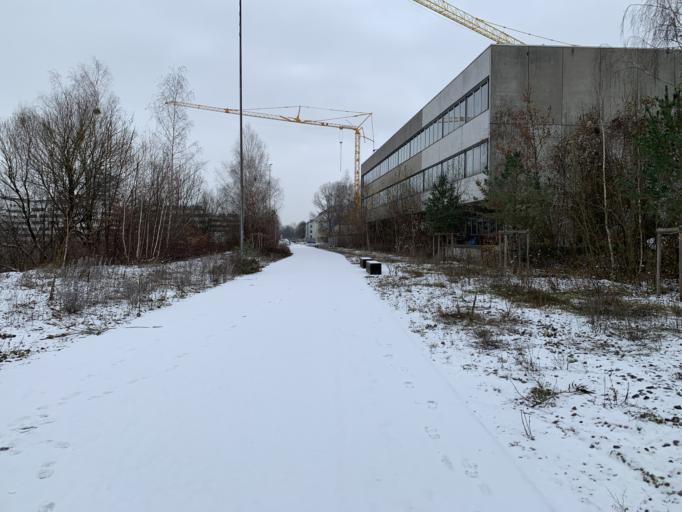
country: DE
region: Bavaria
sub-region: Upper Bavaria
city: Bogenhausen
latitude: 48.1331
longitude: 11.6247
